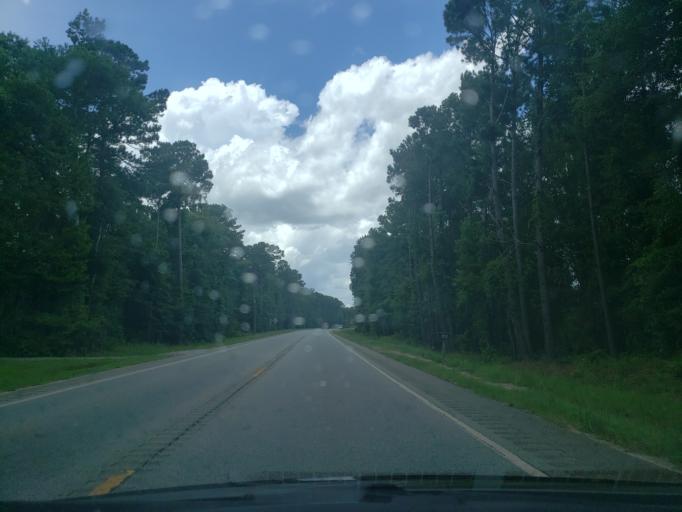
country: US
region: Georgia
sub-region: Bryan County
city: Richmond Hill
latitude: 32.0193
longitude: -81.3122
